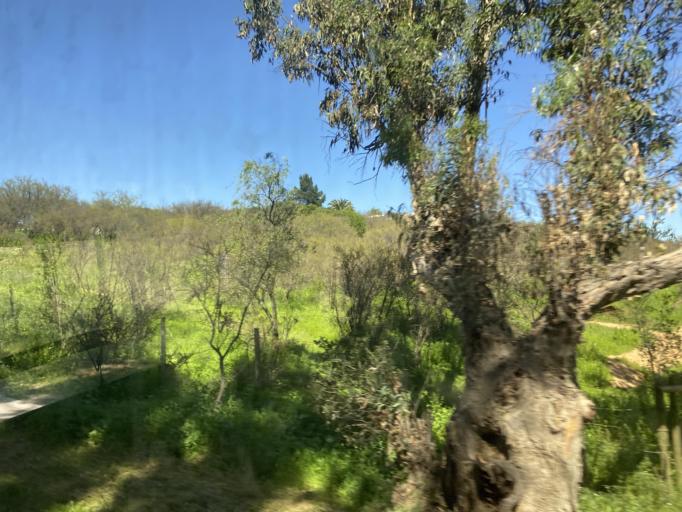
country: CL
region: Valparaiso
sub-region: Provincia de Marga Marga
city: Villa Alemana
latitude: -33.1585
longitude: -71.3271
